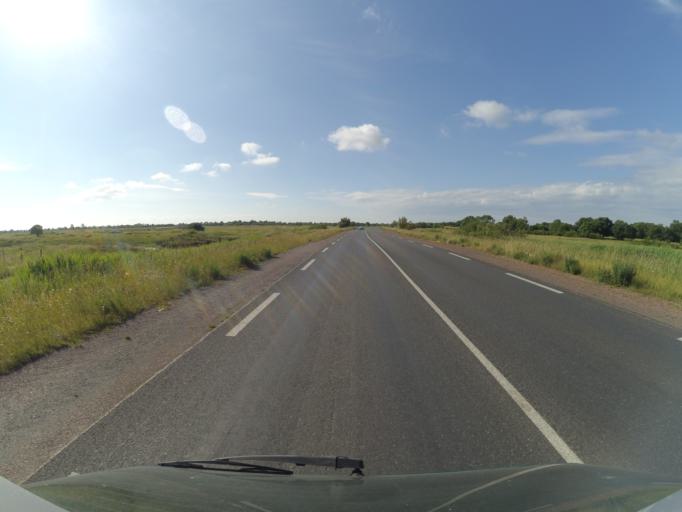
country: FR
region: Poitou-Charentes
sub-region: Departement de la Charente-Maritime
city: Saint-Agnant
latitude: 45.8585
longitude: -0.9660
